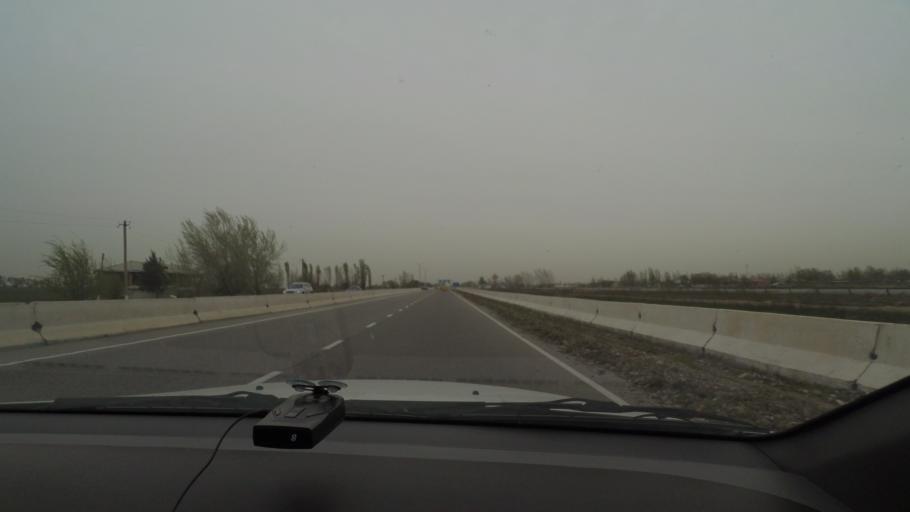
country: UZ
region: Jizzax
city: Gagarin
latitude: 40.4910
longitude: 68.2976
